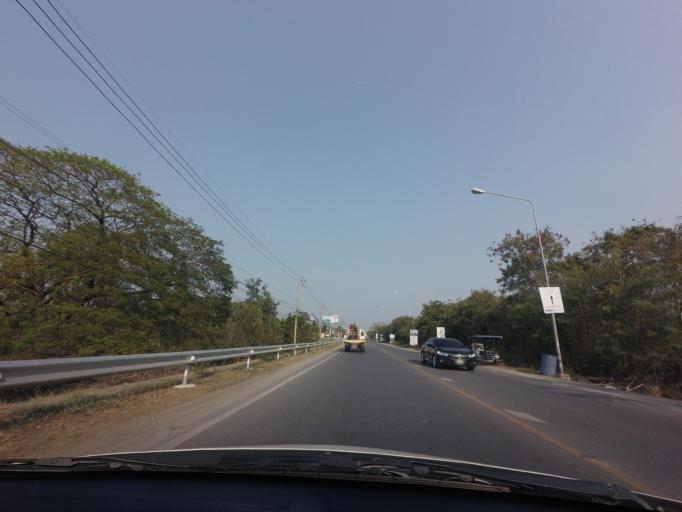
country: TH
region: Nakhon Pathom
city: Salaya
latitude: 13.8124
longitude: 100.3328
